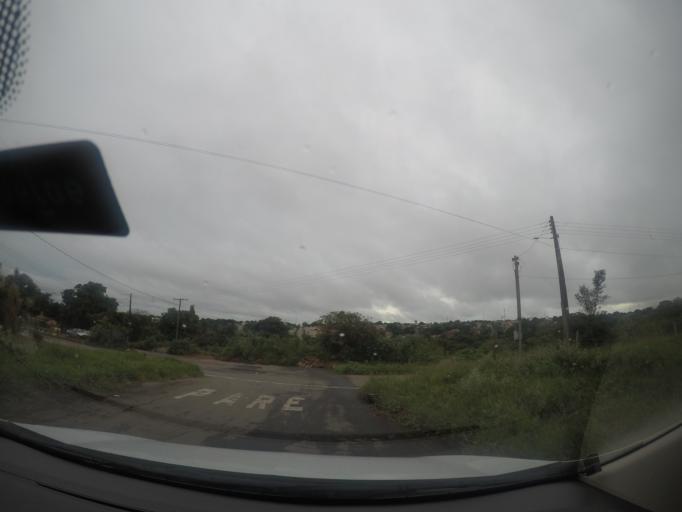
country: BR
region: Goias
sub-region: Aparecida De Goiania
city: Aparecida de Goiania
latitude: -16.7603
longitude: -49.3180
